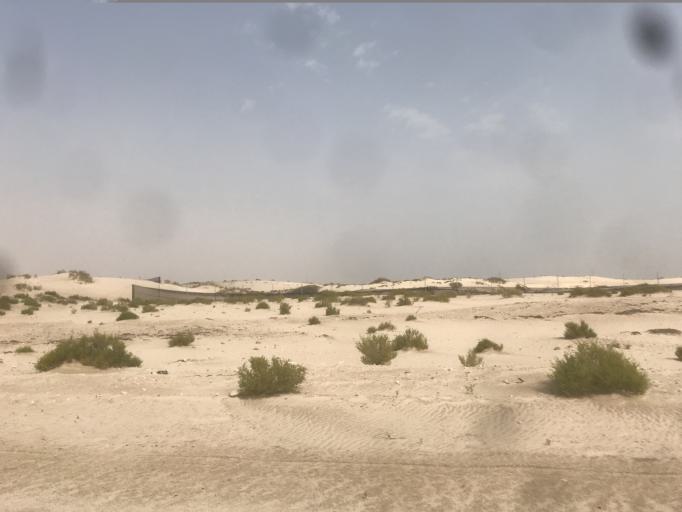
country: SA
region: Eastern Province
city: Abqaiq
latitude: 25.9071
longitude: 49.9983
